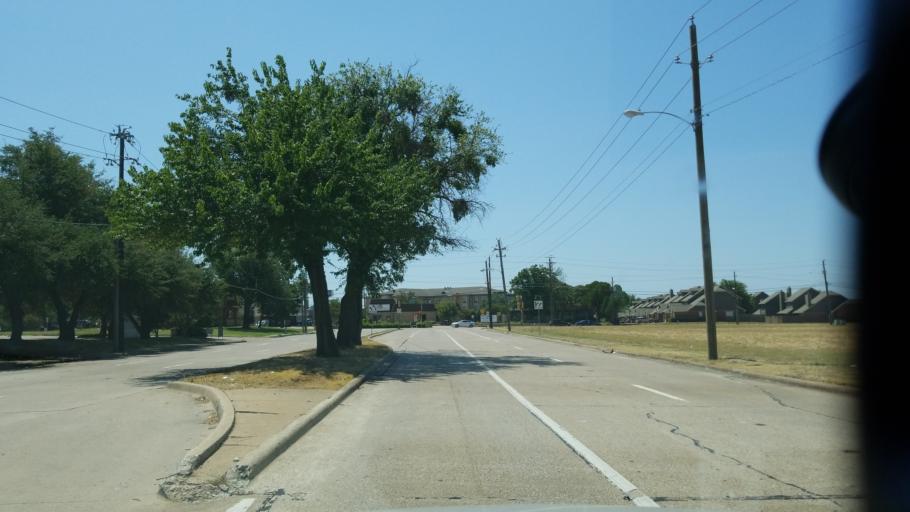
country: US
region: Texas
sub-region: Dallas County
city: Duncanville
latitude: 32.6488
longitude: -96.8876
